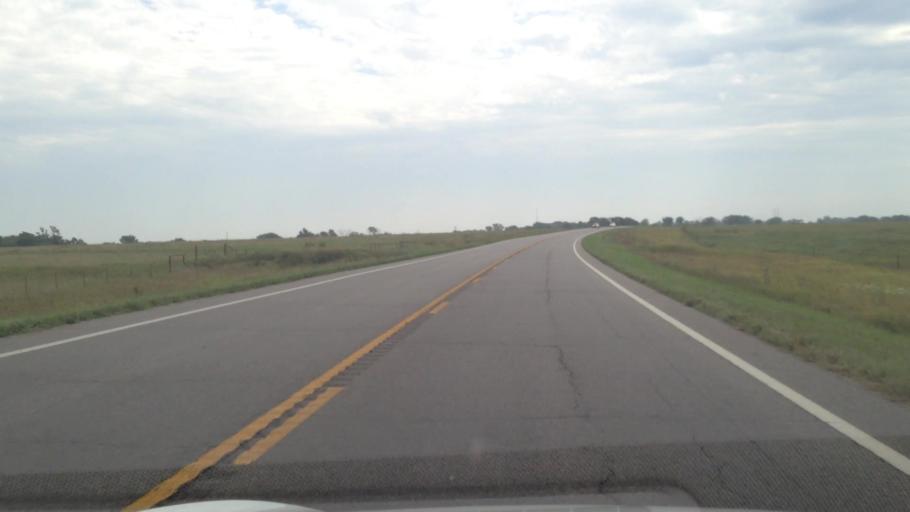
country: US
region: Kansas
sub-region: Bourbon County
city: Fort Scott
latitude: 37.8807
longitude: -95.0093
